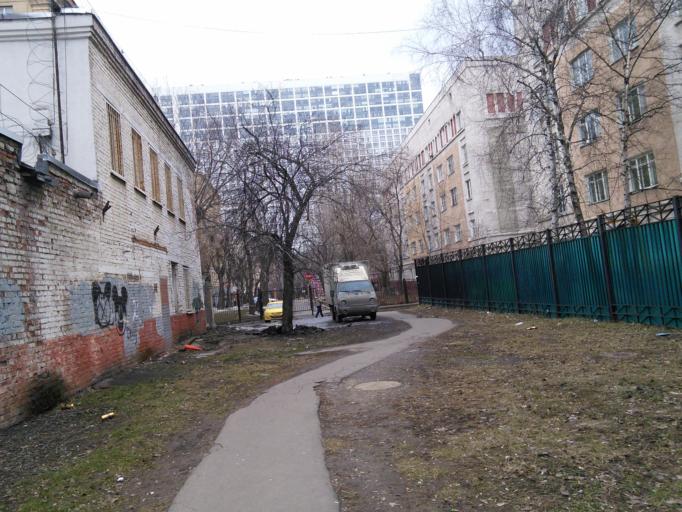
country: RU
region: Moscow
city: Sokol
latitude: 55.8040
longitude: 37.5482
